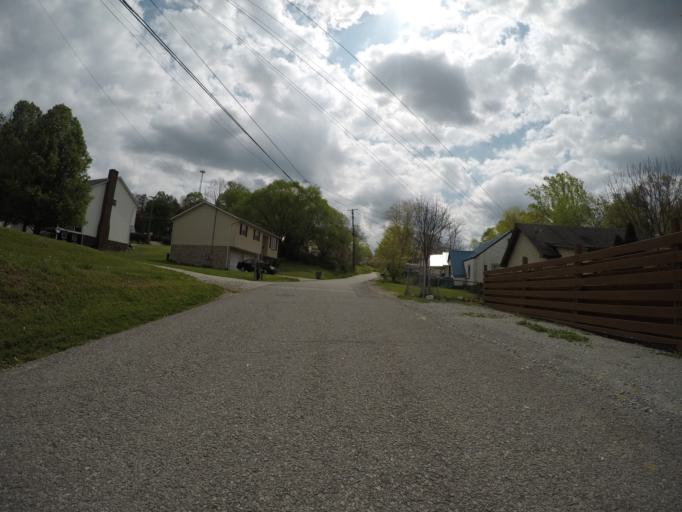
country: US
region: West Virginia
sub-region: Kanawha County
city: Charleston
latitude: 38.3912
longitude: -81.6006
